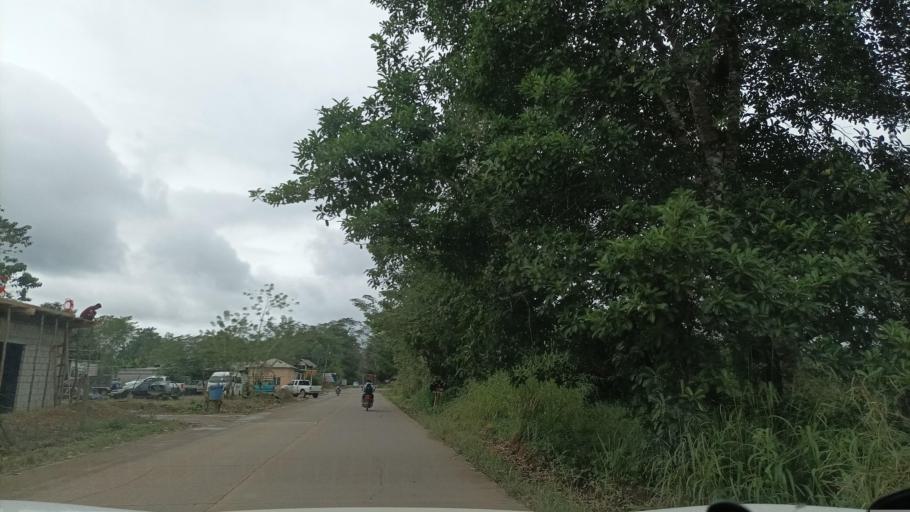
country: MX
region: Veracruz
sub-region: Uxpanapa
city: Poblado 10
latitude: 17.2778
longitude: -94.4692
